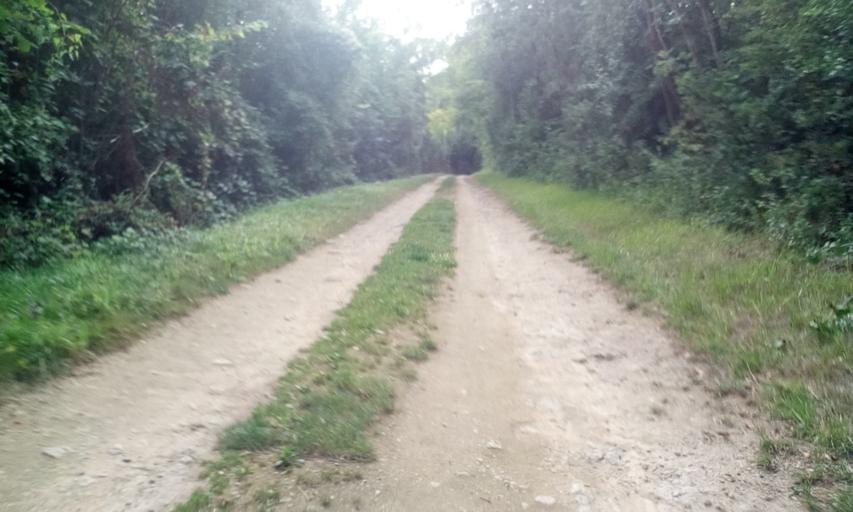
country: FR
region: Lower Normandy
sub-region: Departement du Calvados
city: Cagny
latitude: 49.1041
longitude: -0.2582
